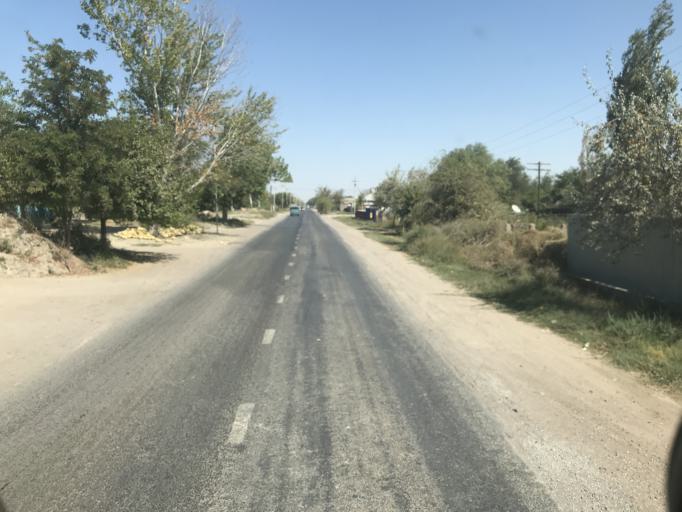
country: KZ
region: Ongtustik Qazaqstan
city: Ilyich
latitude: 40.9288
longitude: 68.4883
